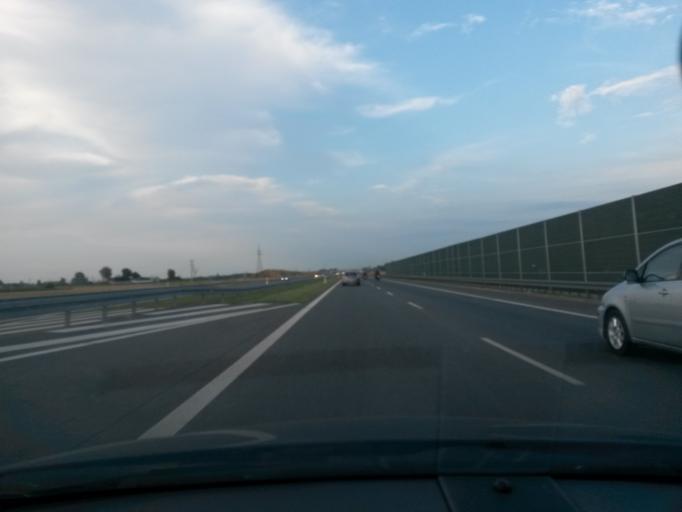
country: PL
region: Masovian Voivodeship
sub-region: Powiat warszawski zachodni
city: Bieniewice
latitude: 52.1326
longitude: 20.5547
